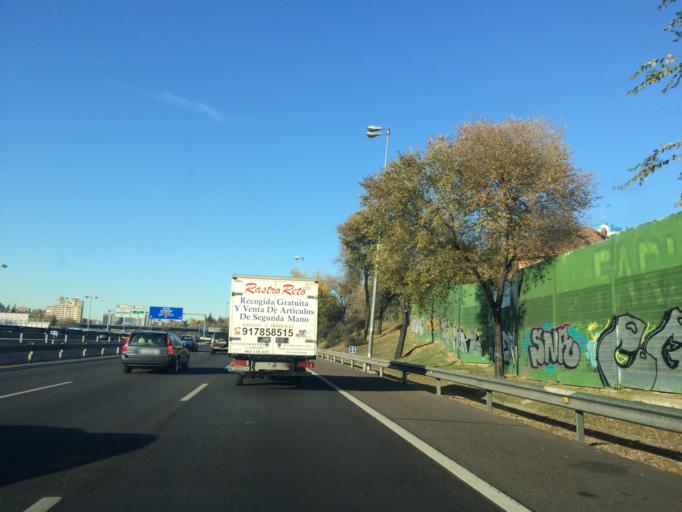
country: ES
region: Madrid
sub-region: Provincia de Madrid
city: Ciudad Lineal
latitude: 40.4551
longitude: -3.6629
